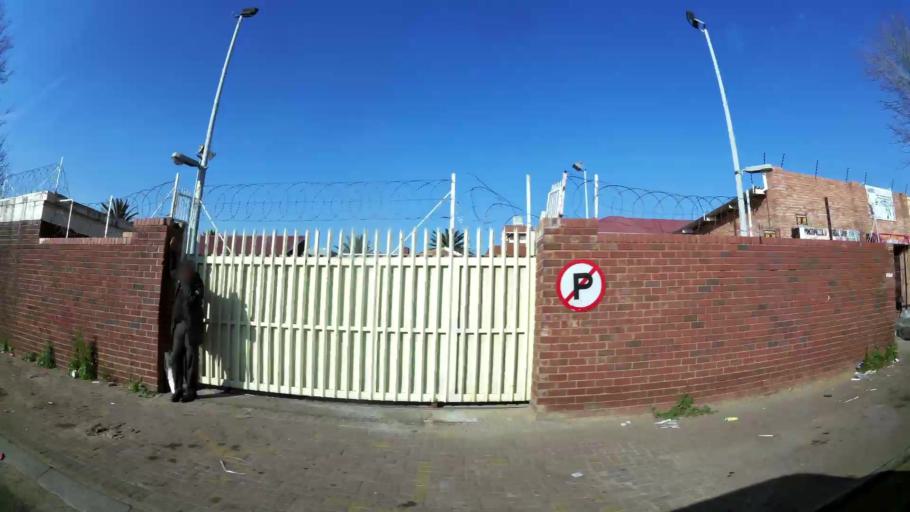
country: ZA
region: Gauteng
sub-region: West Rand District Municipality
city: Randfontein
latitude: -26.1822
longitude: 27.6989
